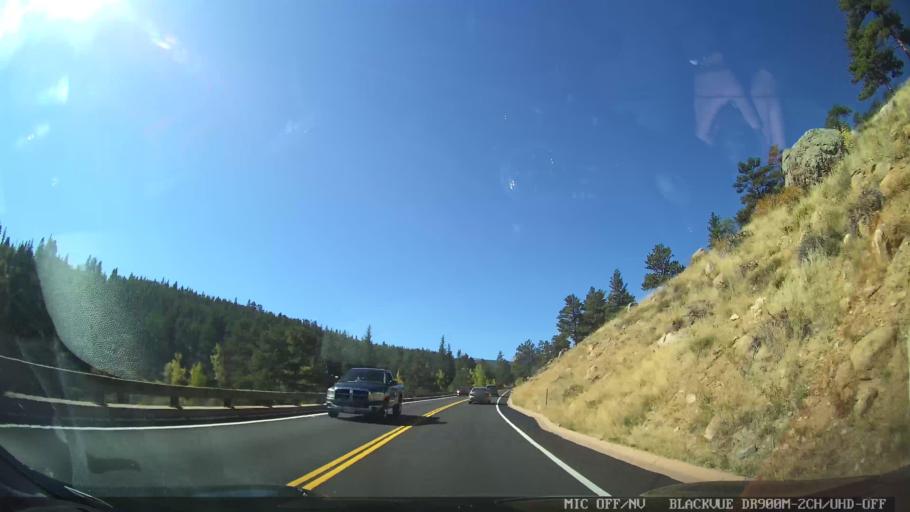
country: US
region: Colorado
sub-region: Larimer County
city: Estes Park
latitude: 40.3445
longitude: -105.5941
